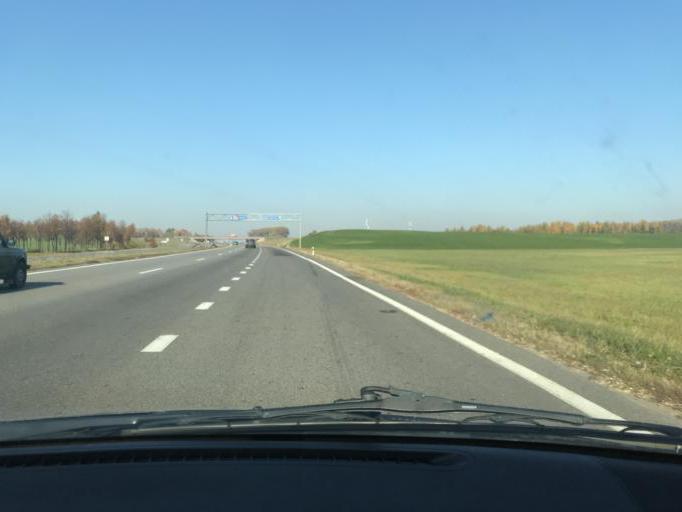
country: BY
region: Minsk
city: Samakhvalavichy
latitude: 53.7210
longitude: 27.5188
